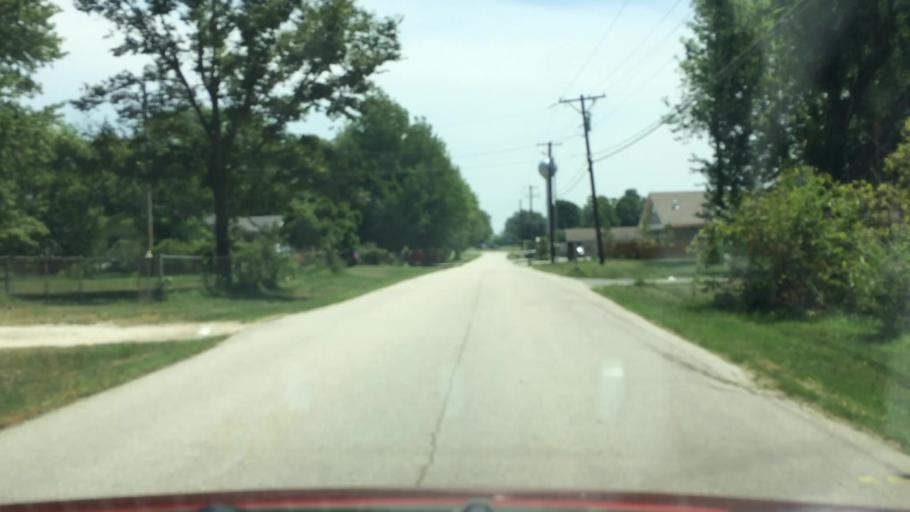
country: US
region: Missouri
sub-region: Greene County
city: Strafford
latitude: 37.2708
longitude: -93.1301
